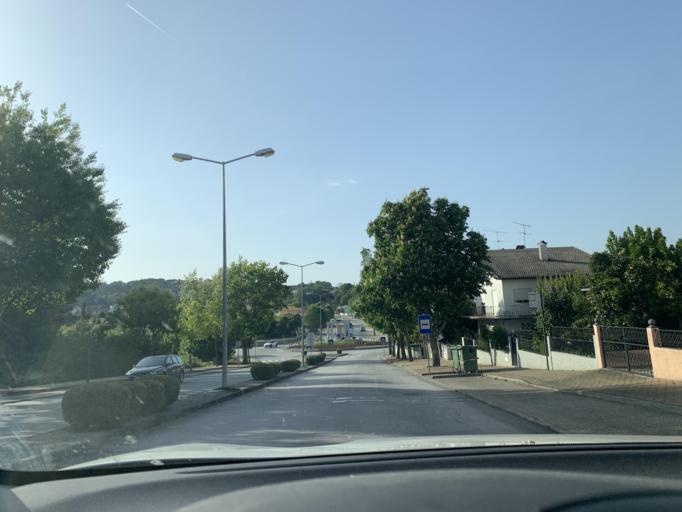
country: PT
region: Viseu
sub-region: Mangualde
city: Mangualde
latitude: 40.5962
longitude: -7.7578
